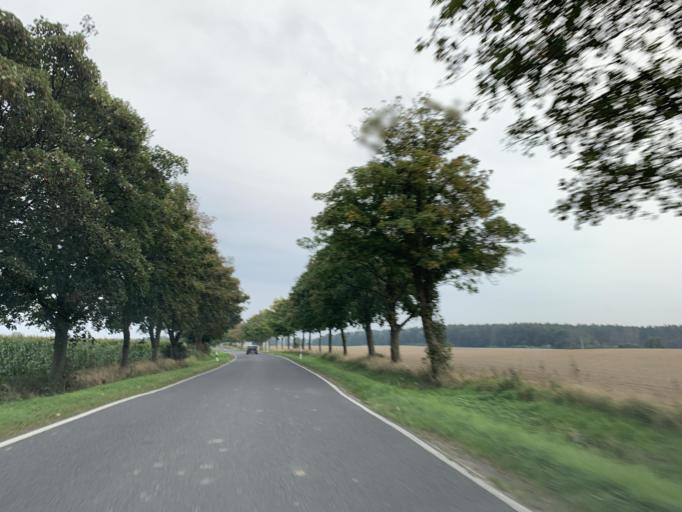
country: DE
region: Mecklenburg-Vorpommern
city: Woldegk
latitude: 53.3293
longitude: 13.5371
